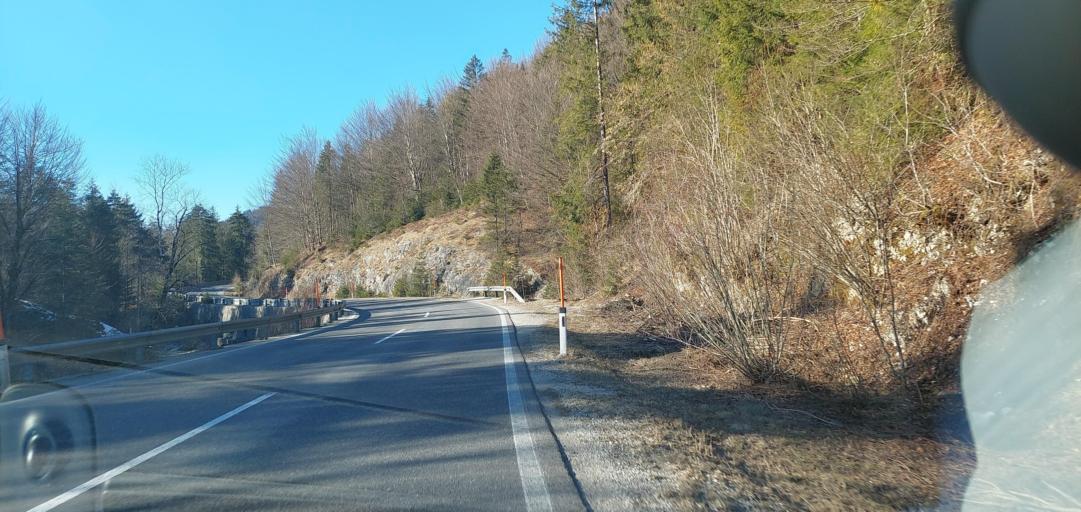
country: AT
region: Upper Austria
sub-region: Politischer Bezirk Gmunden
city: Bad Ischl
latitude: 47.7629
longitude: 13.6489
